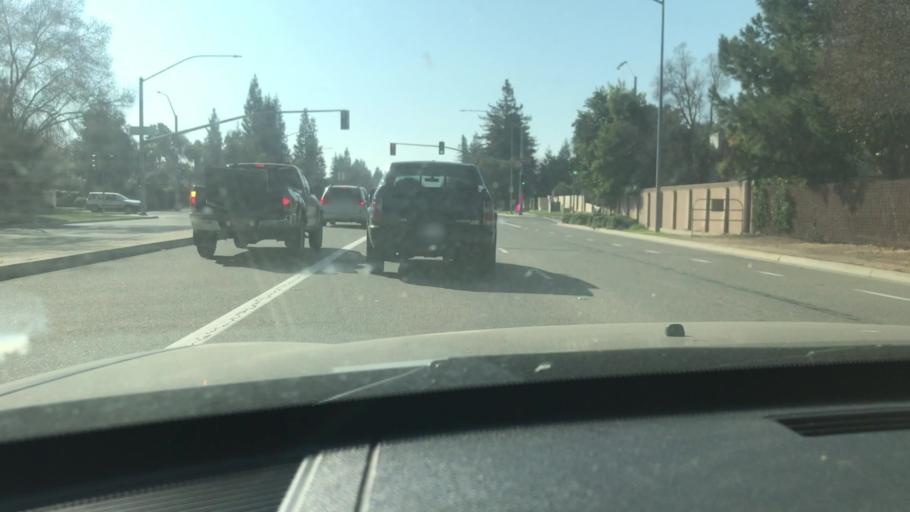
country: US
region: California
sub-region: Fresno County
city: Clovis
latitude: 36.8163
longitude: -119.6640
